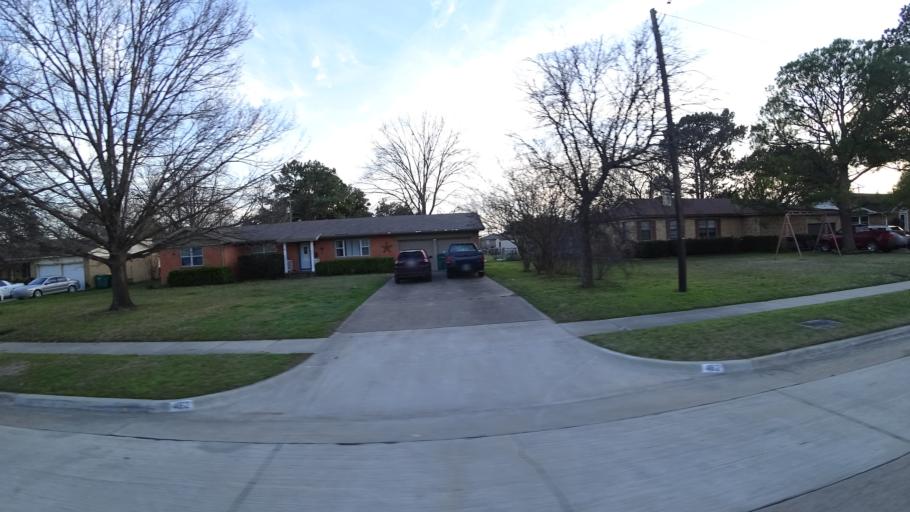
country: US
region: Texas
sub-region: Denton County
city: Lewisville
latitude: 33.0420
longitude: -97.0037
